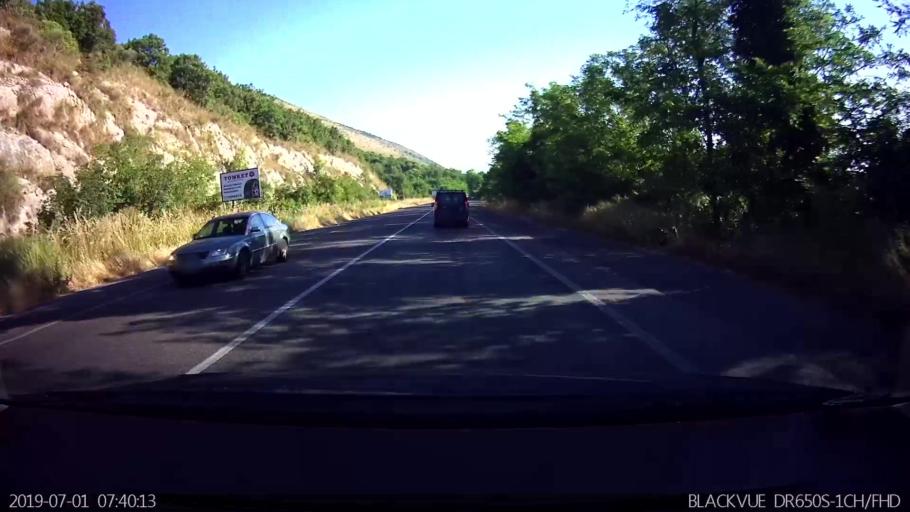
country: IT
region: Latium
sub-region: Provincia di Frosinone
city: Giuliano di Roma
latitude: 41.5558
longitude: 13.2664
